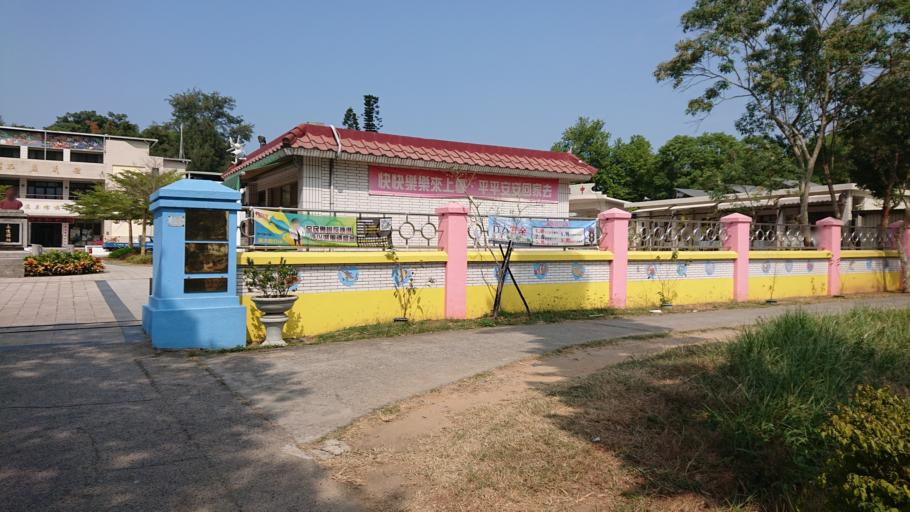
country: TW
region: Fukien
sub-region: Kinmen
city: Jincheng
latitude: 24.4313
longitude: 118.2464
